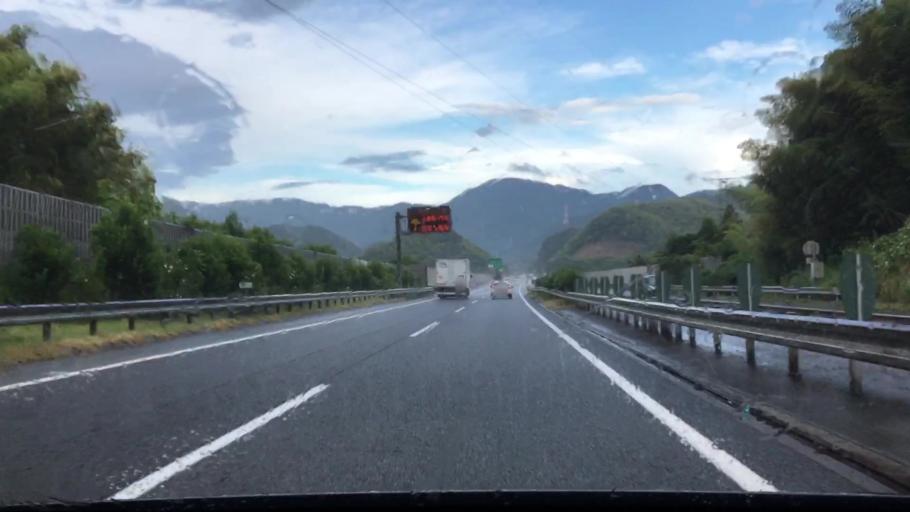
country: JP
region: Fukuoka
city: Kitakyushu
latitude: 33.8062
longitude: 130.8470
